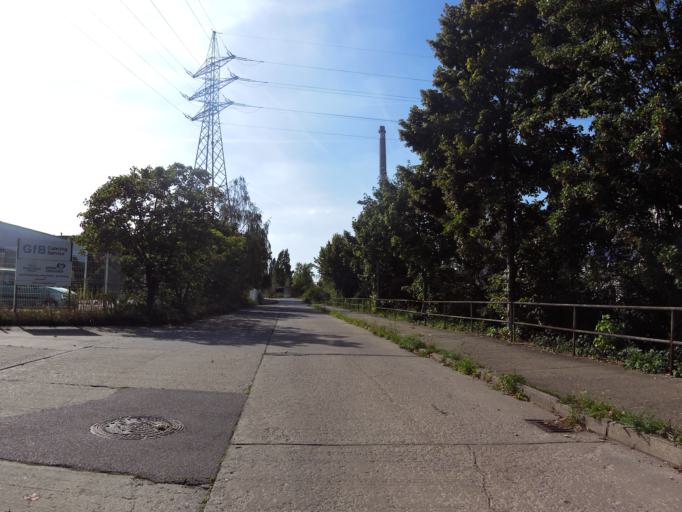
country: DE
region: Saxony
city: Leipzig
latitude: 51.3463
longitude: 12.2996
